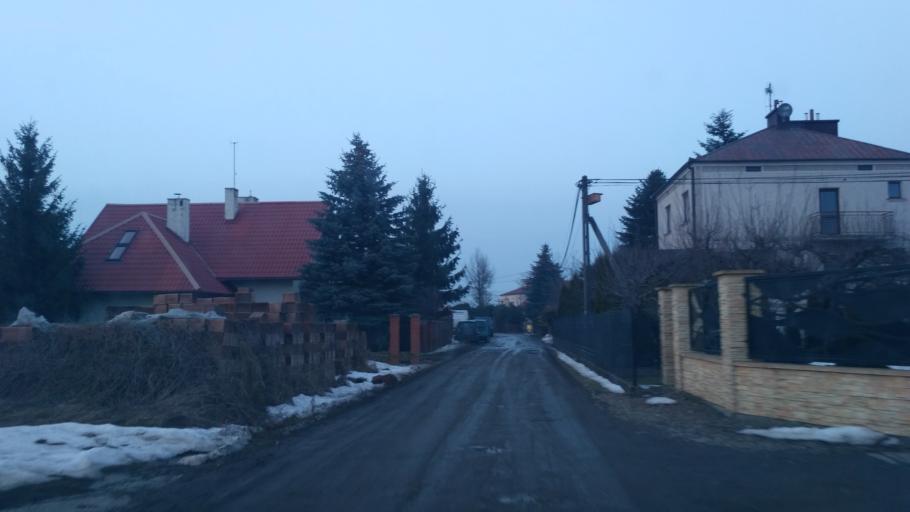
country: PL
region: Subcarpathian Voivodeship
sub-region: Powiat rzeszowski
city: Boguchwala
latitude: 49.9878
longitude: 21.9756
